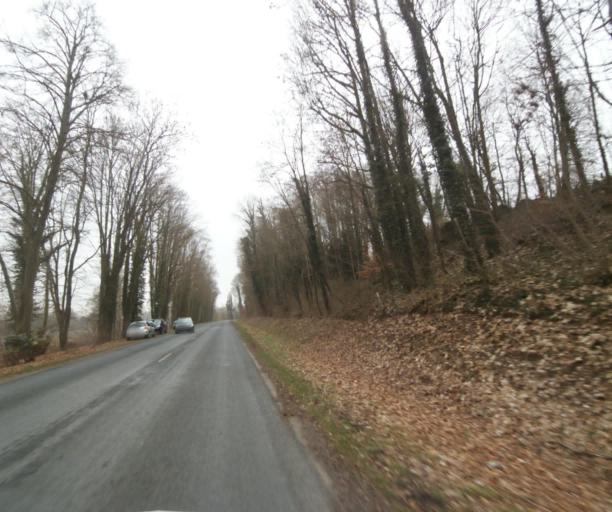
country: FR
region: Champagne-Ardenne
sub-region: Departement de la Haute-Marne
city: Bienville
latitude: 48.5805
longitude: 5.0396
